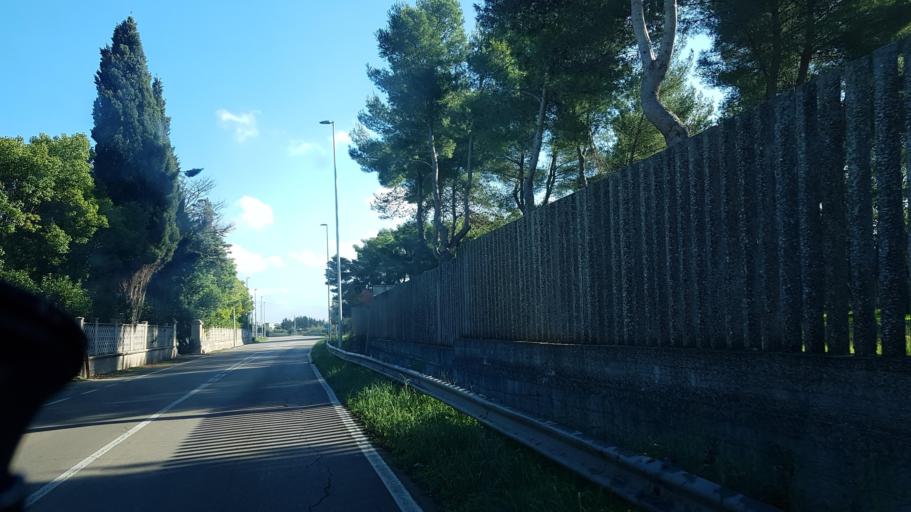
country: IT
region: Apulia
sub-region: Provincia di Lecce
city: Arnesano
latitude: 40.3357
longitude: 18.1011
